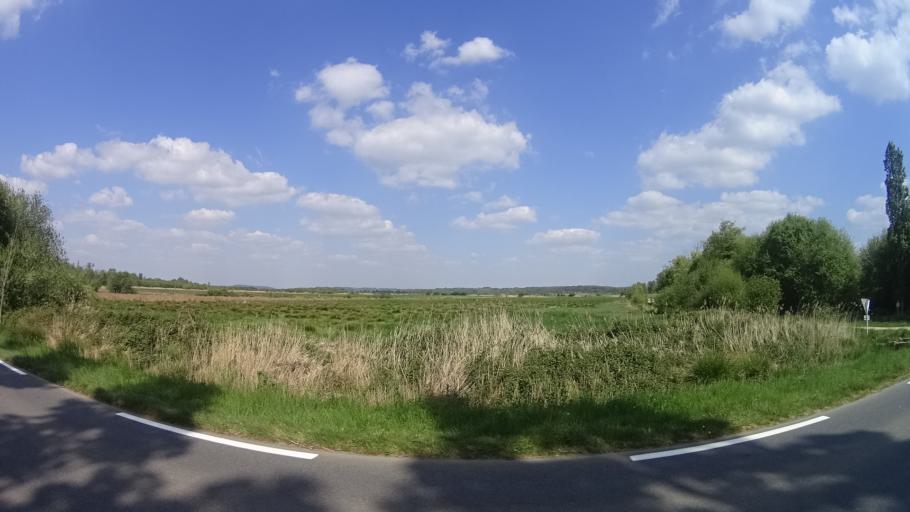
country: FR
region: Brittany
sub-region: Departement du Morbihan
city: Rieux
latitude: 47.6054
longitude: -2.1080
